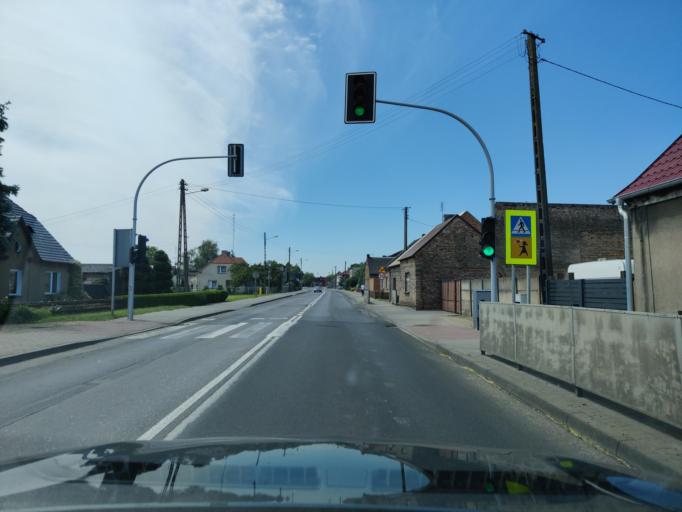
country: PL
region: Greater Poland Voivodeship
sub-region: Powiat grodziski
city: Grodzisk Wielkopolski
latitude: 52.1839
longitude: 16.3360
